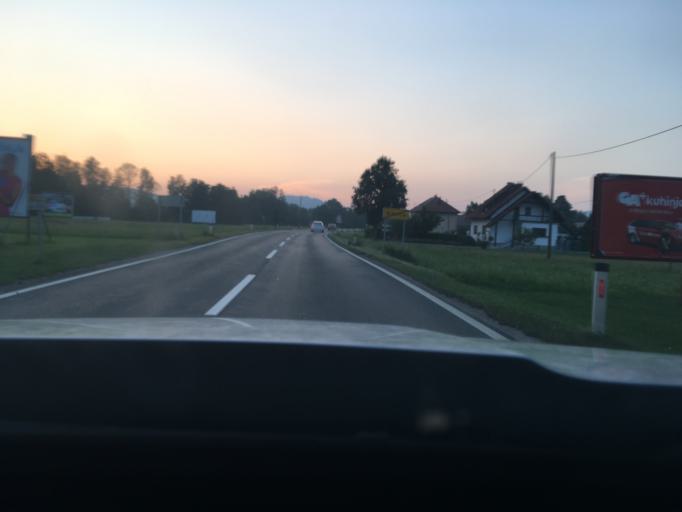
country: SI
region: Ribnica
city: Ribnica
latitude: 45.7453
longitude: 14.7207
